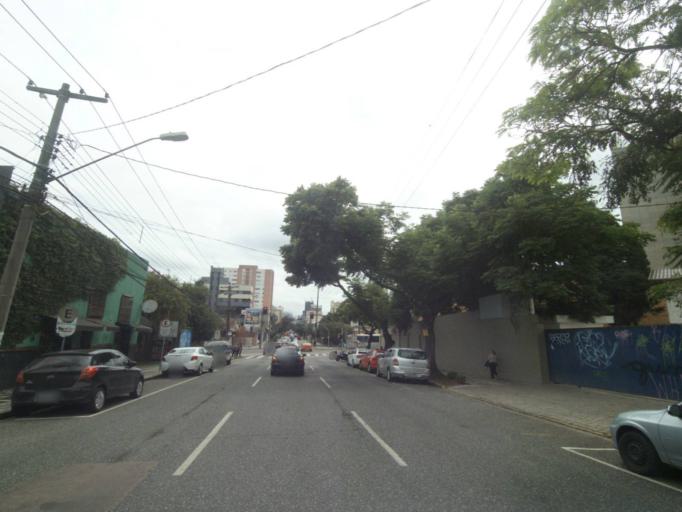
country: BR
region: Parana
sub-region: Curitiba
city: Curitiba
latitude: -25.4304
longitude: -49.2802
